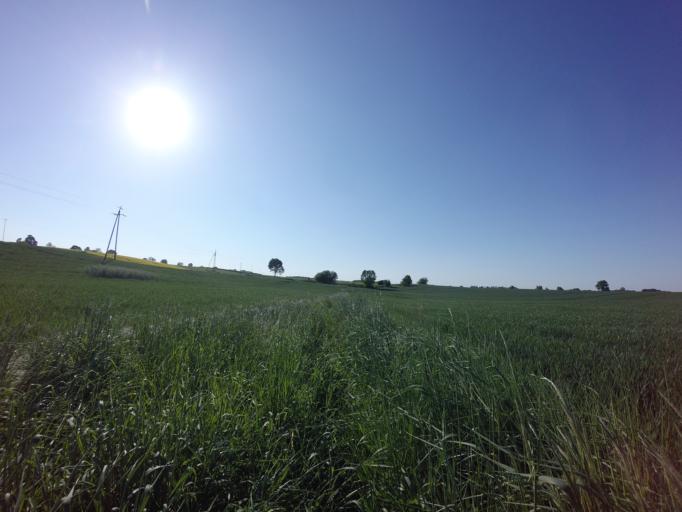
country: PL
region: West Pomeranian Voivodeship
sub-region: Powiat choszczenski
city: Choszczno
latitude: 53.1360
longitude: 15.3700
